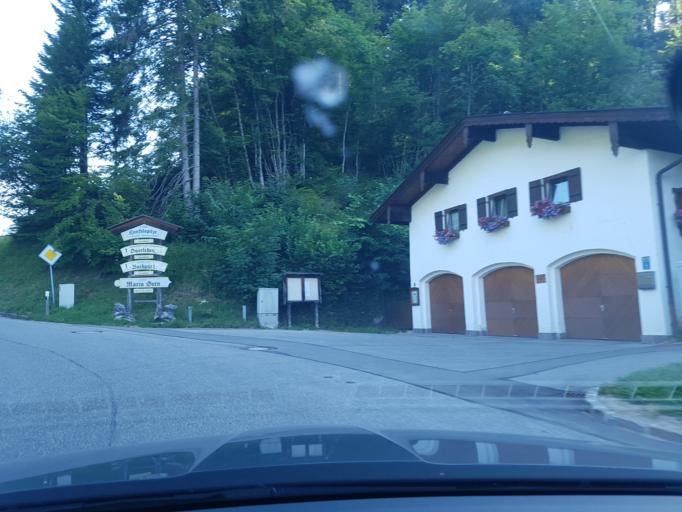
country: DE
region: Bavaria
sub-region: Upper Bavaria
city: Berchtesgaden
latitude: 47.6535
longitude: 13.0029
